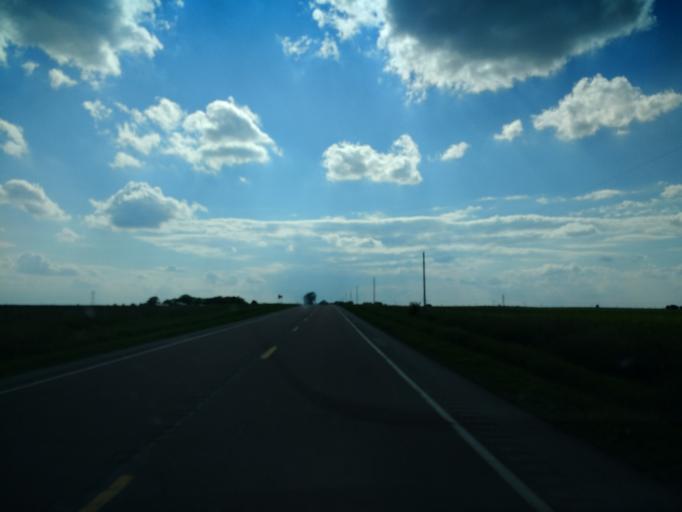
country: US
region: Iowa
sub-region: Clay County
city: Spencer
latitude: 43.1836
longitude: -95.2330
